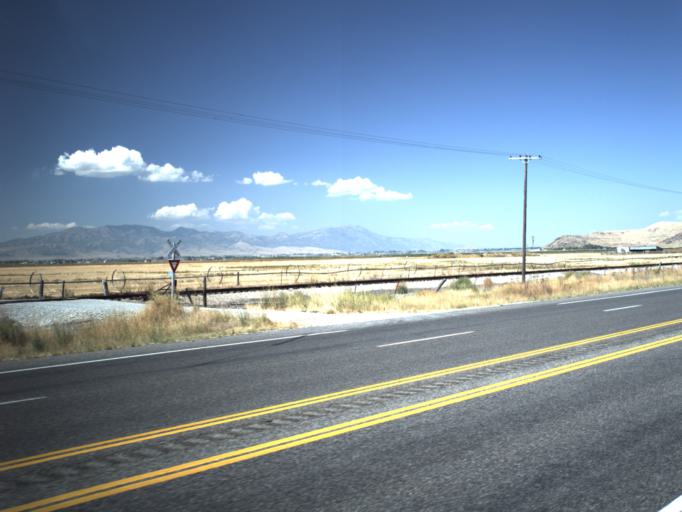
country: US
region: Utah
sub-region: Cache County
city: Lewiston
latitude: 41.9830
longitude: -111.8127
